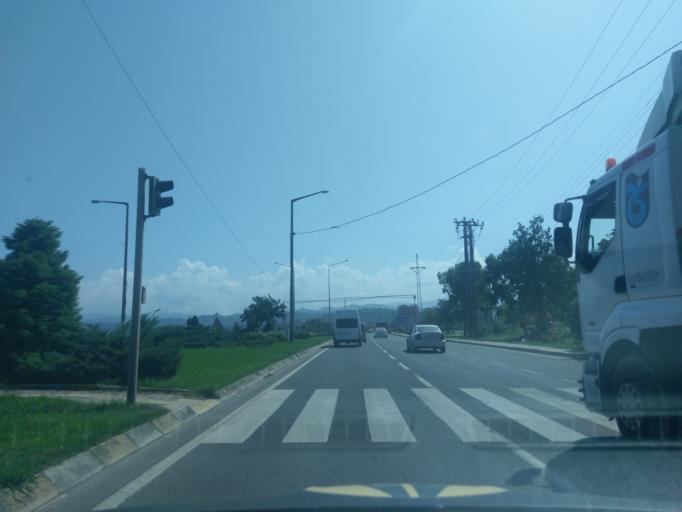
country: TR
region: Ordu
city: Fatsa
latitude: 41.0247
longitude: 37.5227
